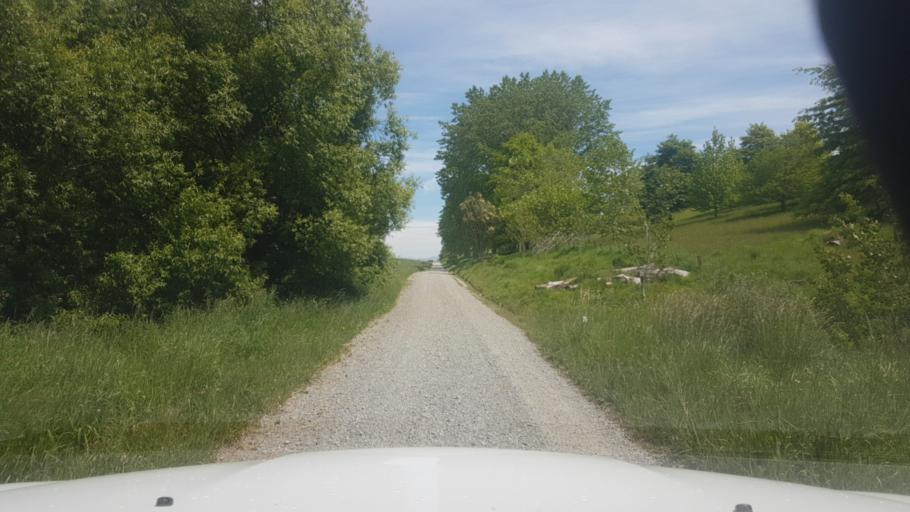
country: NZ
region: Canterbury
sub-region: Timaru District
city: Pleasant Point
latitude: -44.1974
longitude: 171.1149
